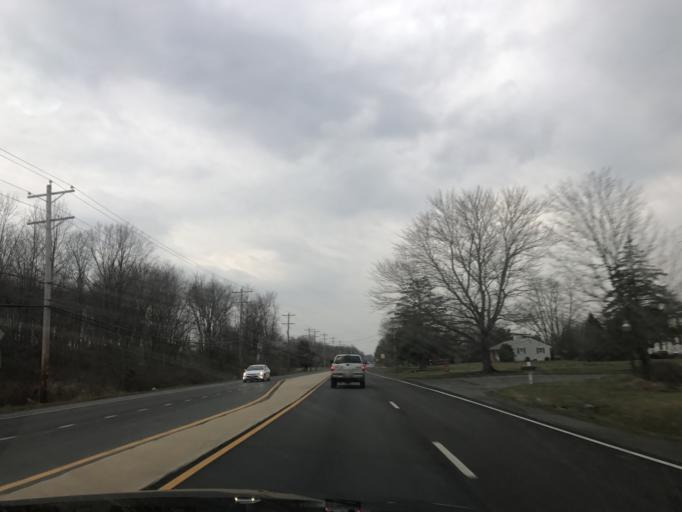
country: US
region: Delaware
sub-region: New Castle County
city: Glasgow
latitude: 39.6257
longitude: -75.7742
